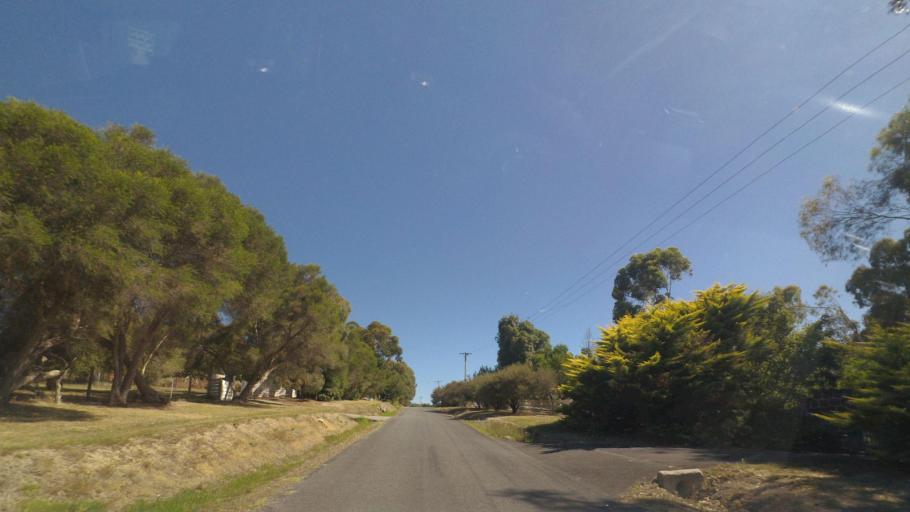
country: AU
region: Victoria
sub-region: Yarra Ranges
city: Chirnside Park
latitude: -37.7382
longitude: 145.3334
